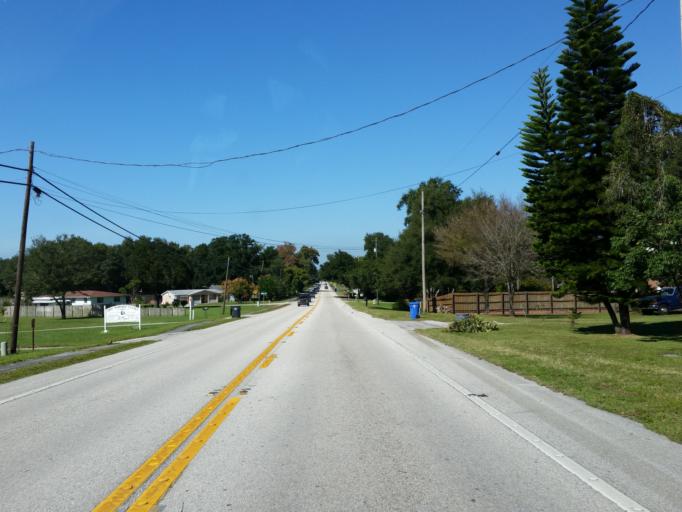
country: US
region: Florida
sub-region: Hillsborough County
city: Bloomingdale
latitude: 27.9123
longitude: -82.2602
